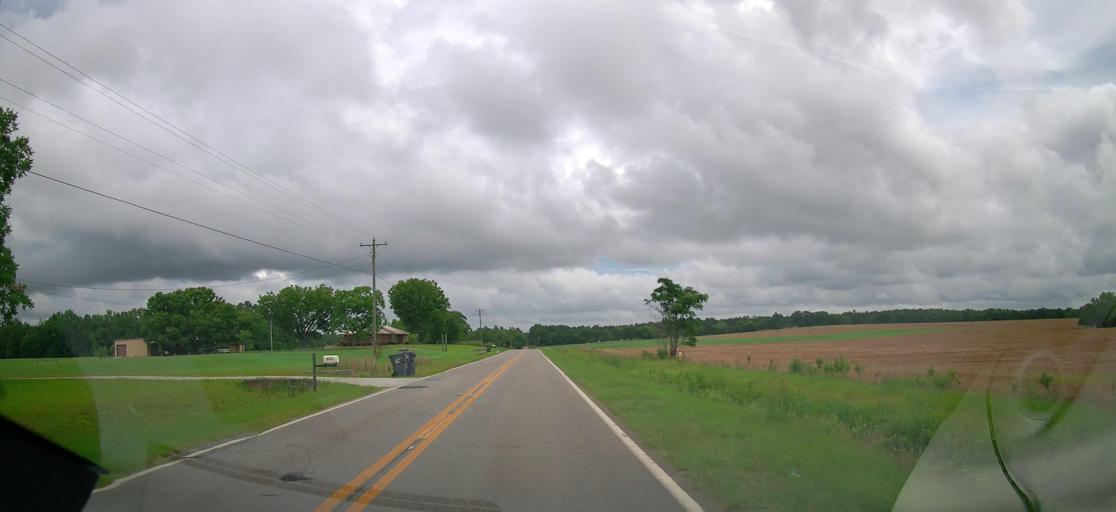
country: US
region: Georgia
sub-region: Bibb County
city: West Point
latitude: 32.7338
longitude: -83.7658
